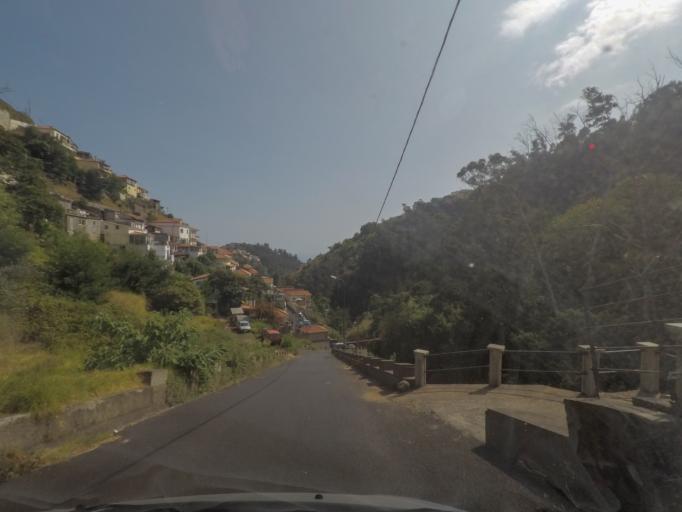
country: PT
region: Madeira
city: Camara de Lobos
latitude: 32.6751
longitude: -16.9519
